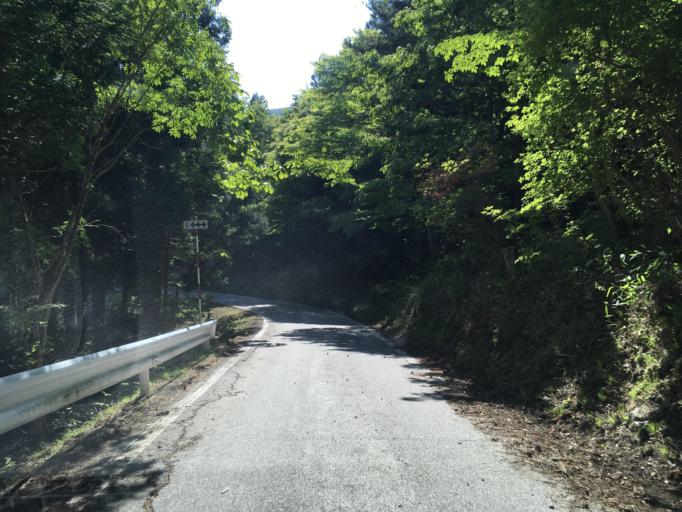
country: JP
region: Iwate
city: Ofunato
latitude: 39.1825
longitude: 141.7543
